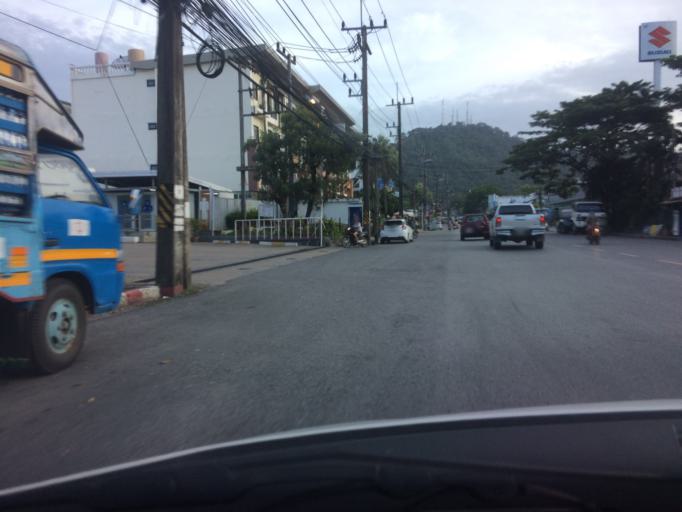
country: TH
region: Phuket
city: Ban Talat Yai
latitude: 7.8830
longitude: 98.3998
